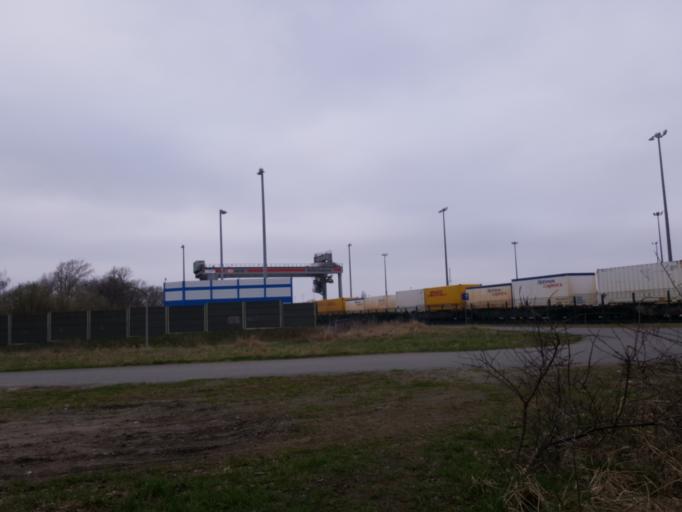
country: DE
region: Hamburg
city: Wandsbek
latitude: 53.5104
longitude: 10.1018
